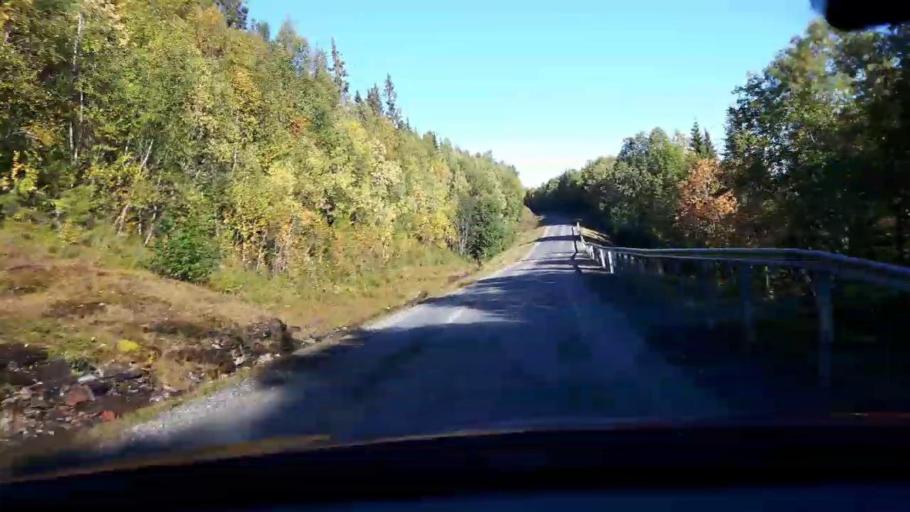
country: NO
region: Nord-Trondelag
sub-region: Lierne
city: Sandvika
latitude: 64.5701
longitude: 13.9035
